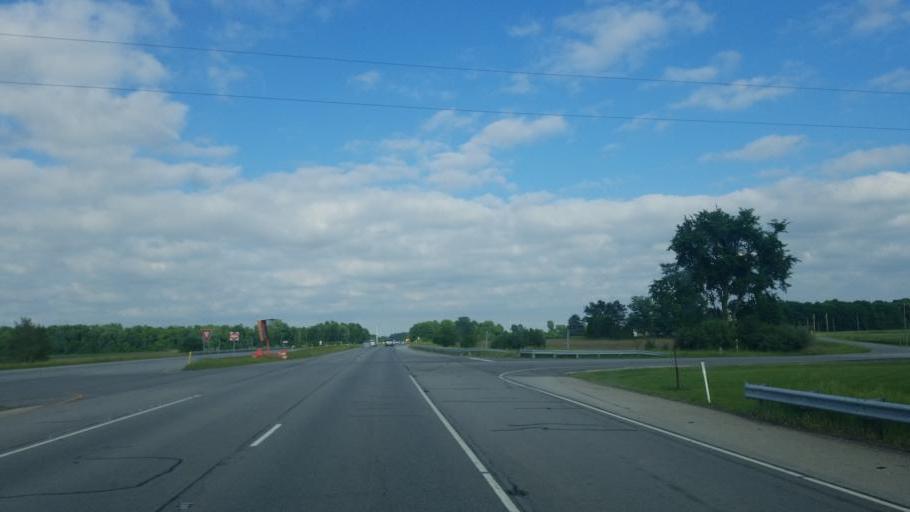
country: US
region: Indiana
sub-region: Whitley County
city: Churubusco
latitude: 41.1258
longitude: -85.2852
